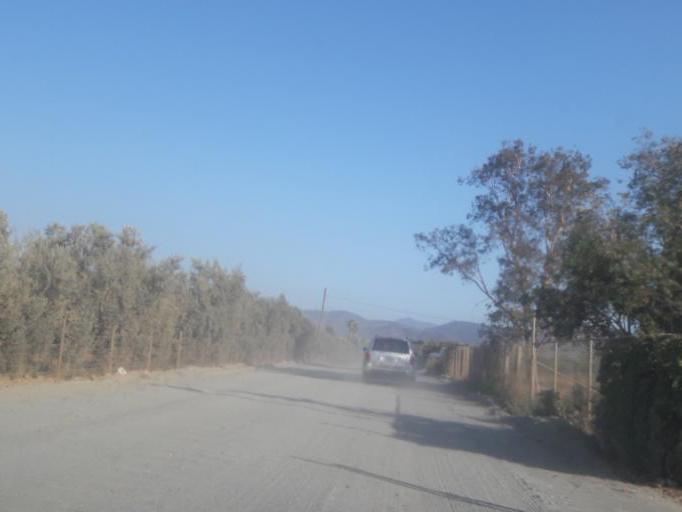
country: MX
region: Baja California
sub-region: Ensenada
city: Rancho Verde
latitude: 32.0870
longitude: -116.6269
